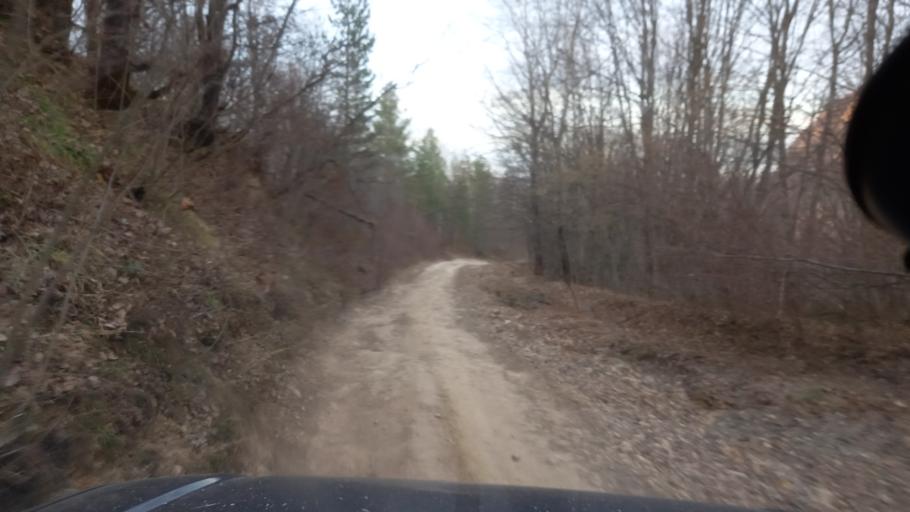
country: RU
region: Krasnodarskiy
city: Neftegorsk
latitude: 44.2191
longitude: 39.9037
